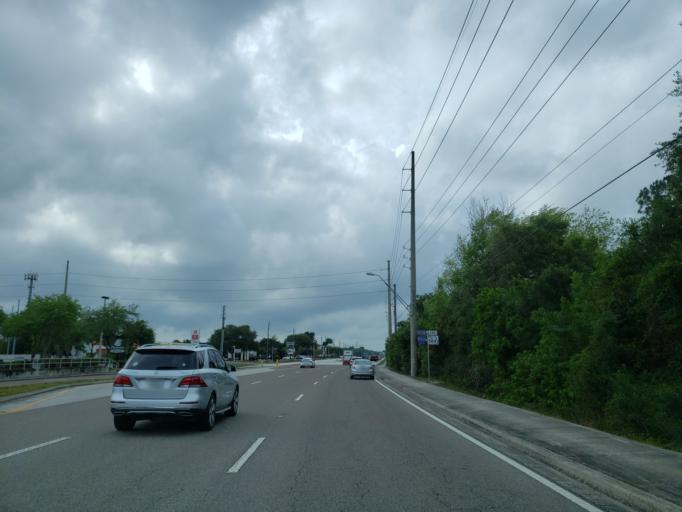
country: US
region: Florida
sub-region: Pinellas County
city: Oldsmar
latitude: 28.0495
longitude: -82.6947
